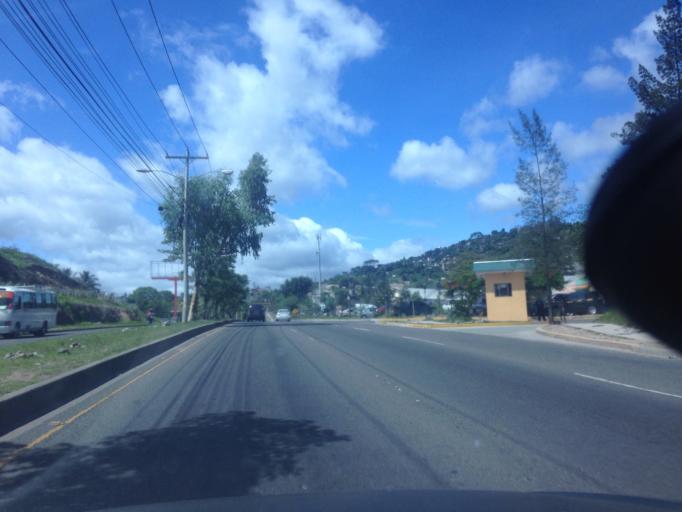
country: HN
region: Francisco Morazan
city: El Tablon
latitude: 14.0577
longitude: -87.1784
